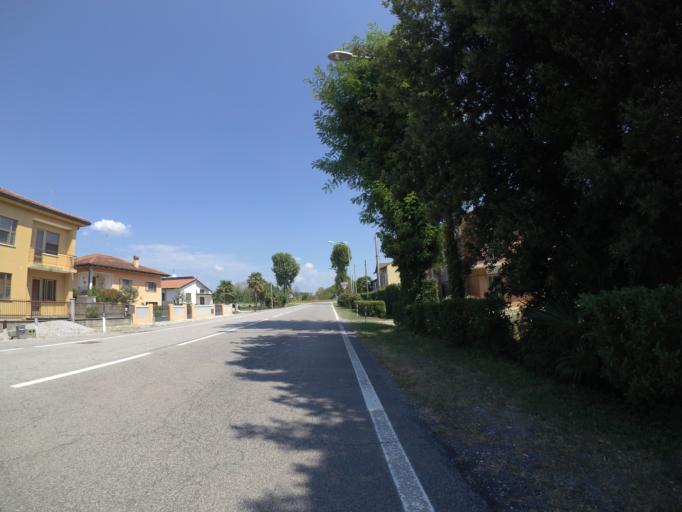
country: IT
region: Friuli Venezia Giulia
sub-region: Provincia di Udine
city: Codroipo
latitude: 45.9672
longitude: 13.0096
